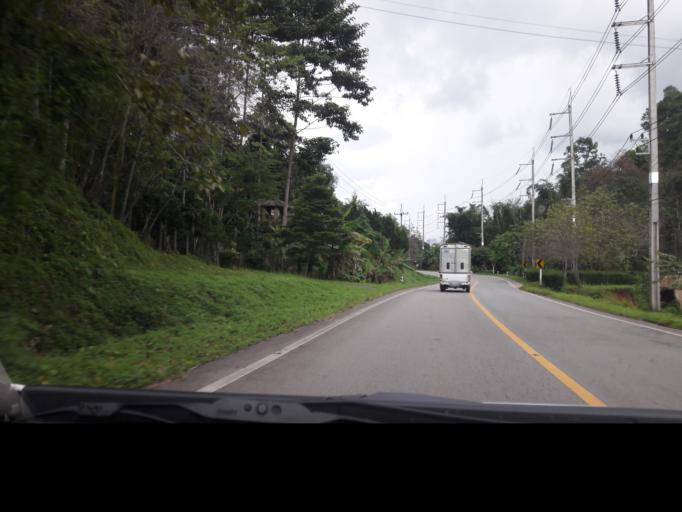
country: TH
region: Chiang Mai
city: Mae Taeng
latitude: 19.1672
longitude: 98.6913
